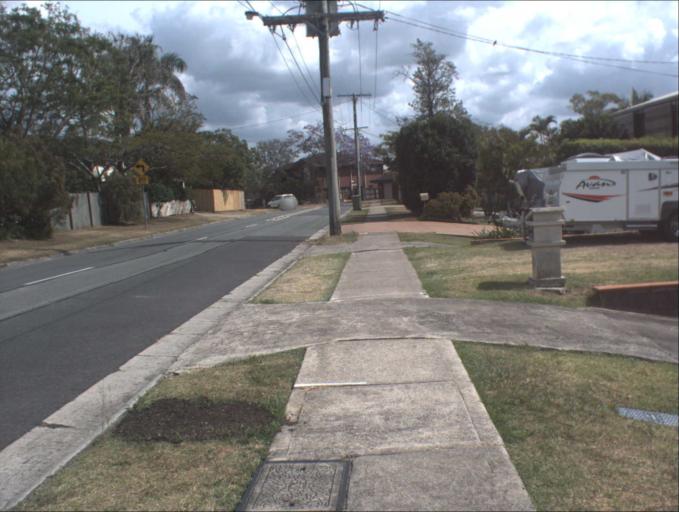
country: AU
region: Queensland
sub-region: Logan
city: Windaroo
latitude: -27.7218
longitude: 153.1938
